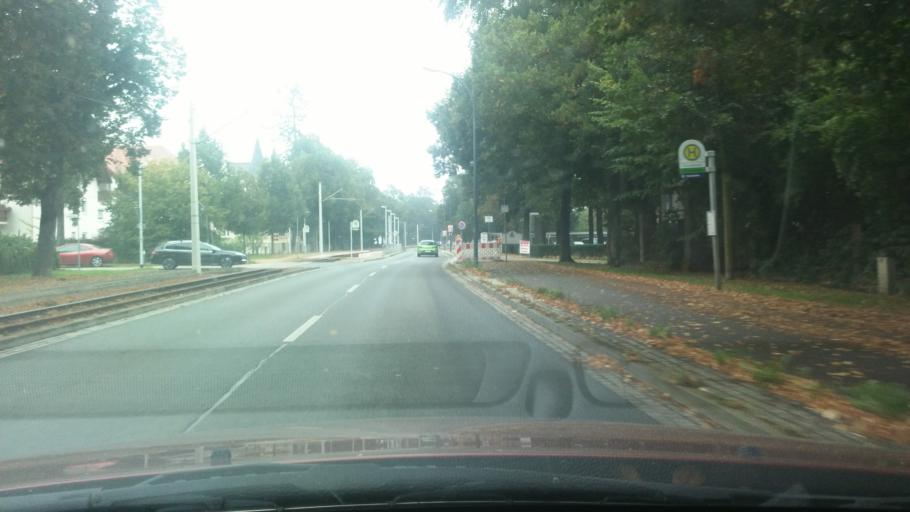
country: DE
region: Saxony
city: Goerlitz
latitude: 51.1360
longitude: 14.9497
